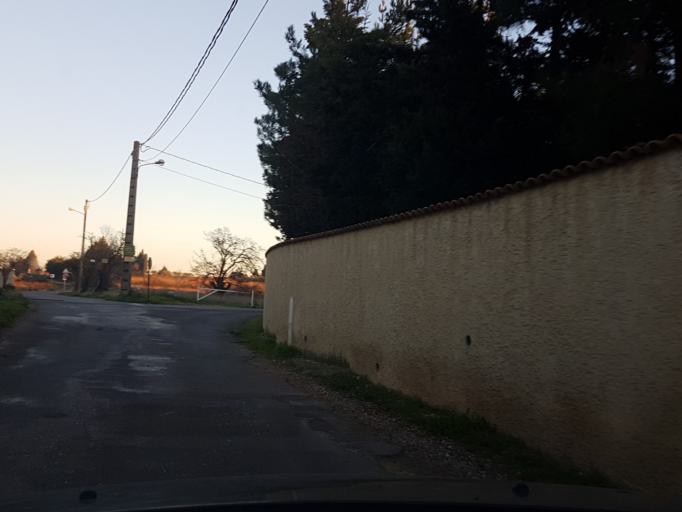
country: FR
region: Provence-Alpes-Cote d'Azur
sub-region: Departement du Vaucluse
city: Vedene
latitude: 43.9664
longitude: 4.9035
